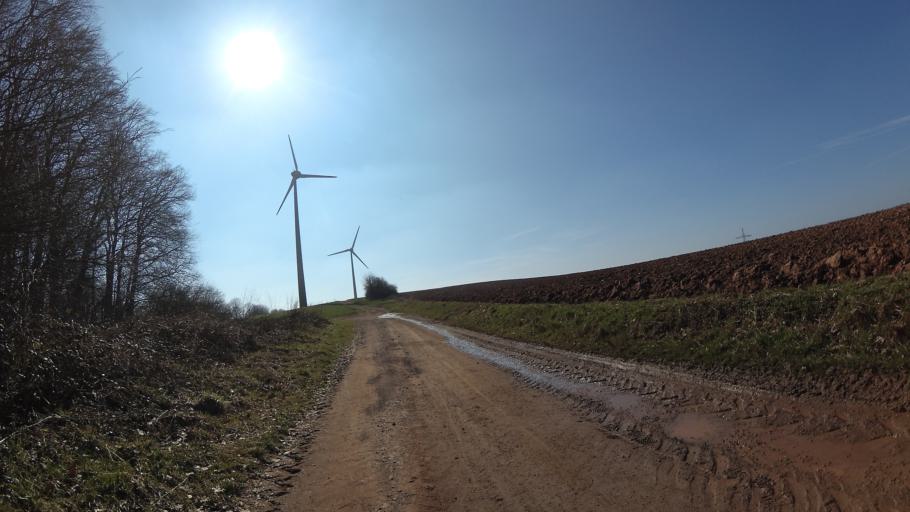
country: DE
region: Saarland
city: Eppelborn
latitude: 49.4339
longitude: 6.9774
